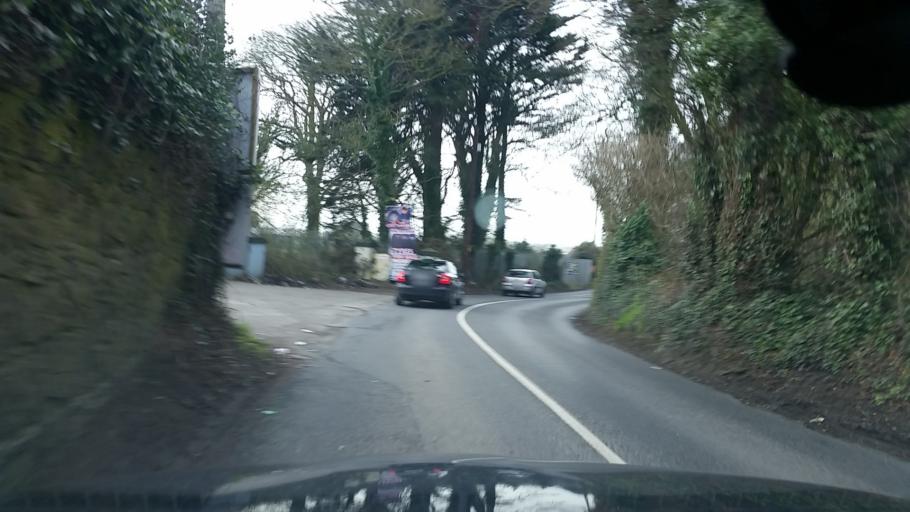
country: IE
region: Leinster
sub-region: Fingal County
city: Blanchardstown
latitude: 53.4103
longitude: -6.3899
